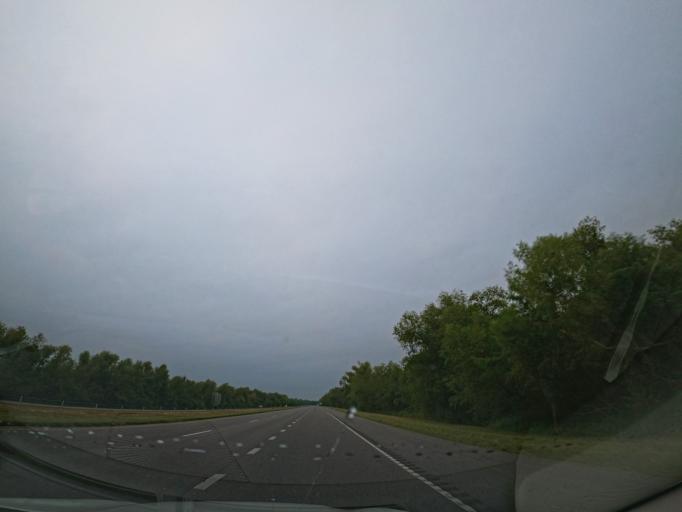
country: US
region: Louisiana
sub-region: Lafourche Parish
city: Raceland
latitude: 29.7033
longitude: -90.5765
